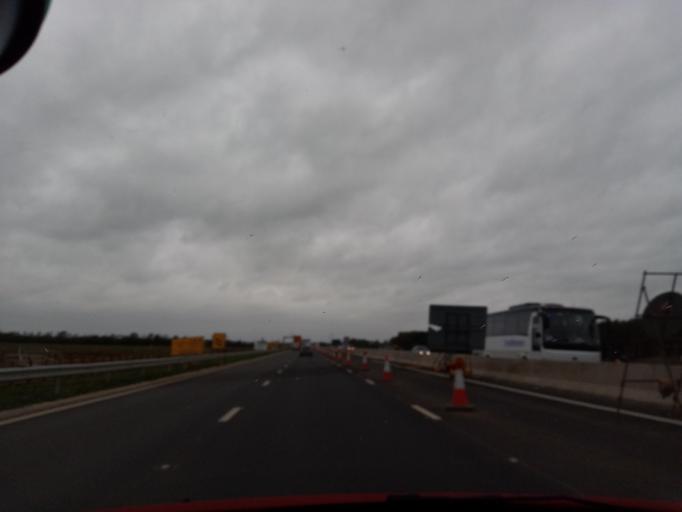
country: GB
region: England
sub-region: Cambridgeshire
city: Swavesey
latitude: 52.2666
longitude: 0.0019
